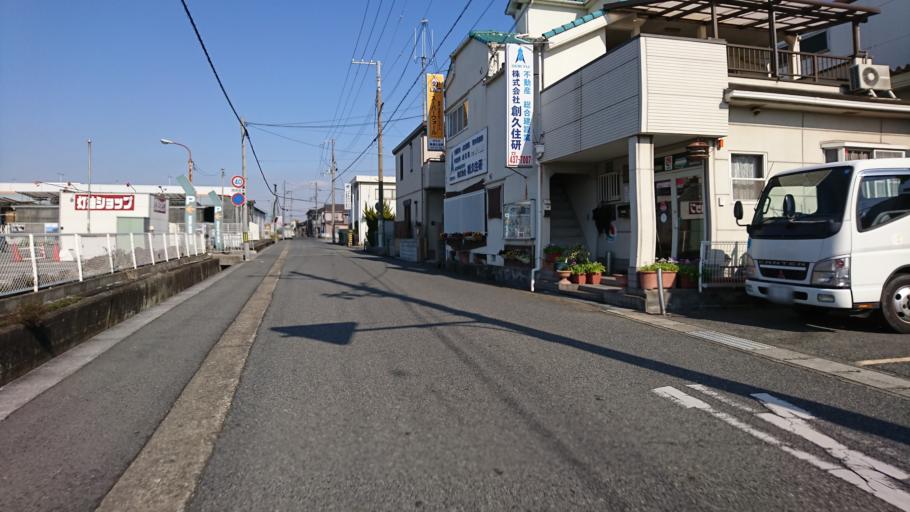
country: JP
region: Hyogo
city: Kakogawacho-honmachi
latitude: 34.7380
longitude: 134.8568
